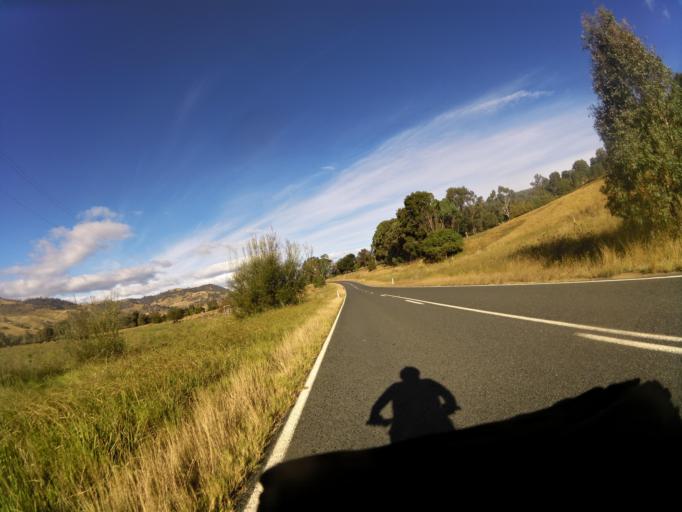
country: AU
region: New South Wales
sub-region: Greater Hume Shire
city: Holbrook
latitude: -35.9702
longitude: 147.7829
